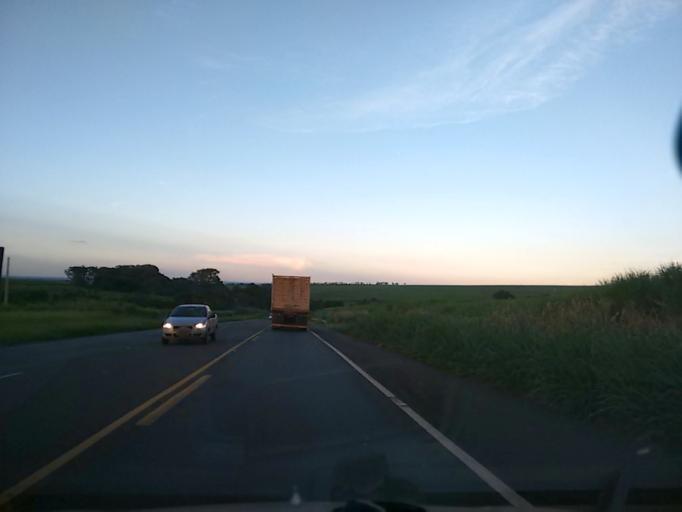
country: BR
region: Sao Paulo
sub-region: Jau
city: Jau
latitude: -22.1501
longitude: -48.4694
